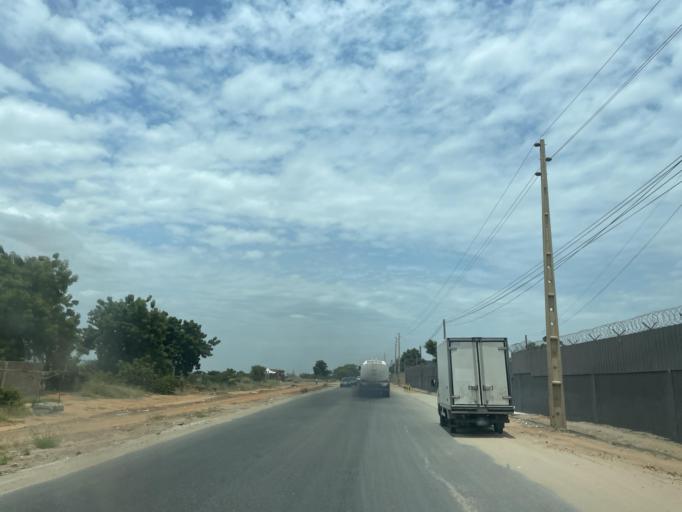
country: AO
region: Luanda
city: Luanda
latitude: -8.9405
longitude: 13.3877
